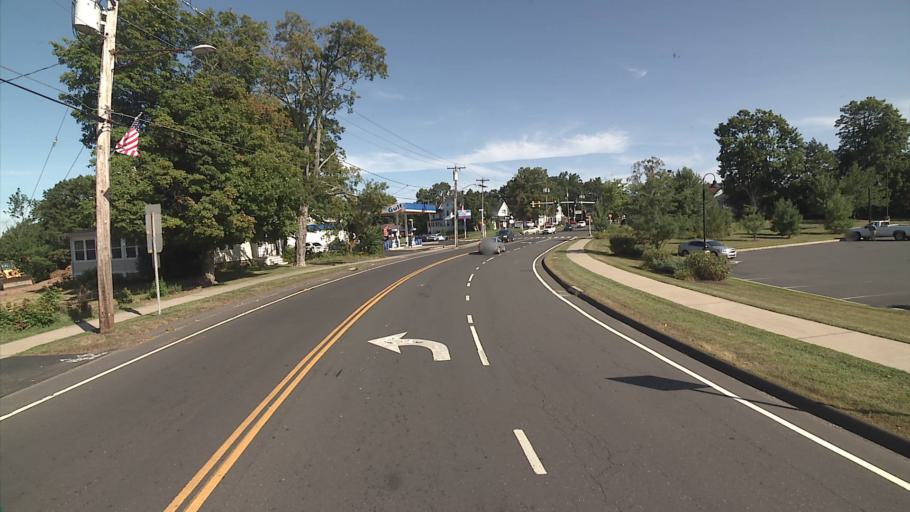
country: US
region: Connecticut
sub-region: New Haven County
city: Cheshire Village
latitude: 41.5035
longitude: -72.9039
